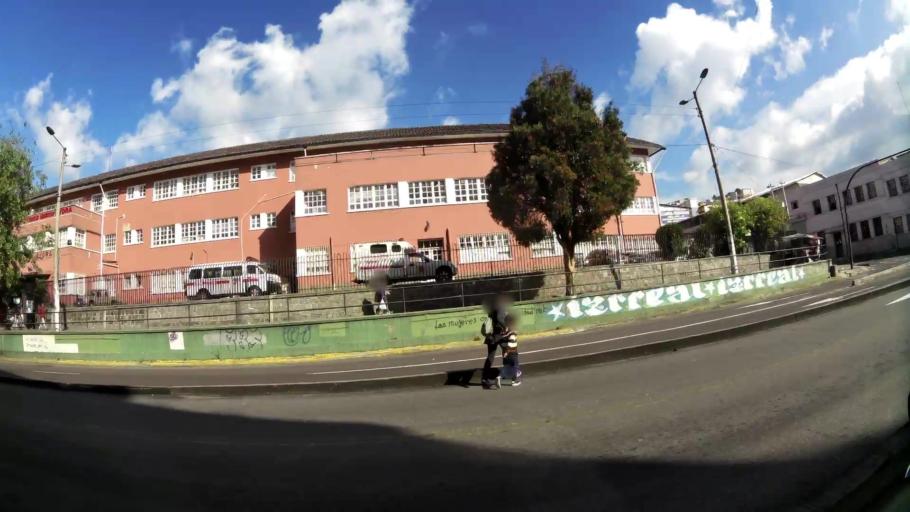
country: EC
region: Pichincha
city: Quito
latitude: -0.2147
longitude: -78.5001
